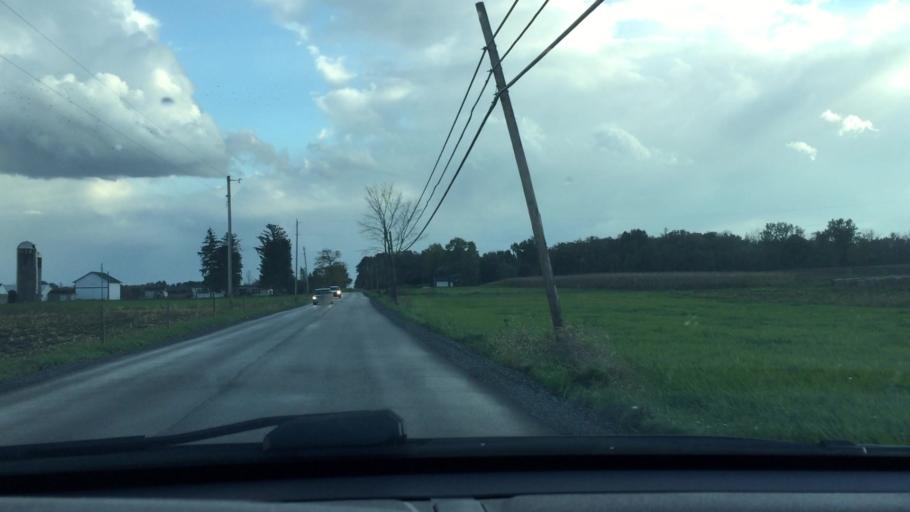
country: US
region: Pennsylvania
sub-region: Lawrence County
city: Bessemer
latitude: 40.9984
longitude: -80.4568
